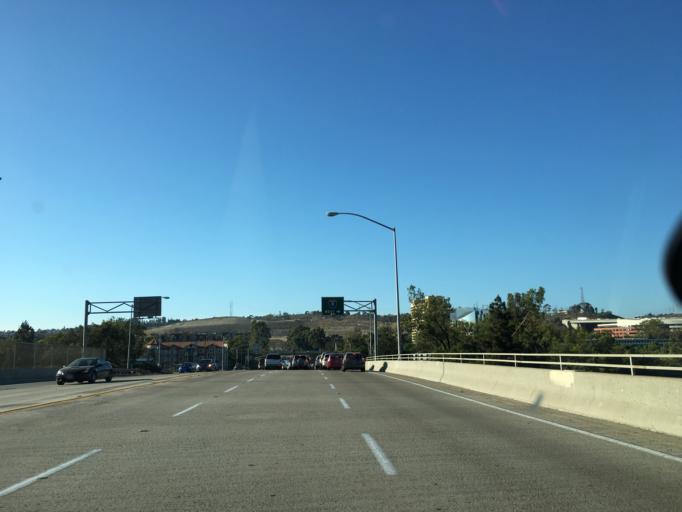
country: US
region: California
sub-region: San Diego County
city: San Diego
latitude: 32.7699
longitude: -117.1397
